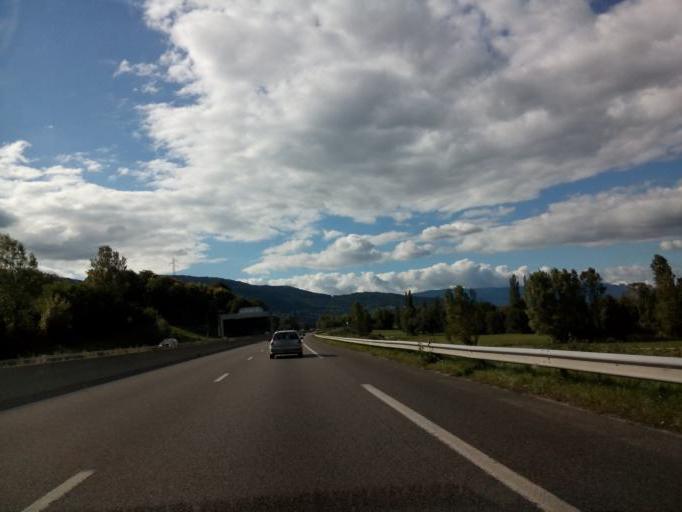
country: FR
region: Rhone-Alpes
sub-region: Departement de la Savoie
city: Les Marches
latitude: 45.5175
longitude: 5.9885
